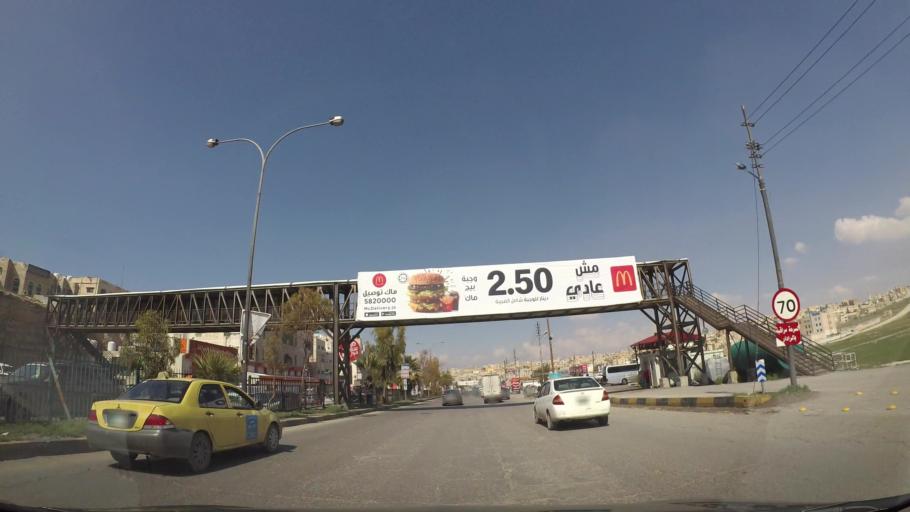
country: JO
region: Zarqa
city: Zarqa
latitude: 32.0360
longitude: 36.0917
